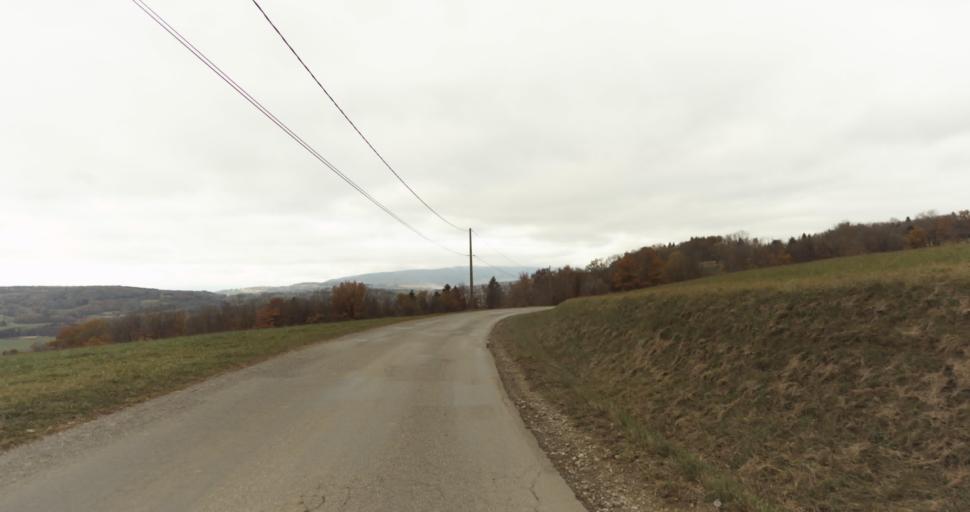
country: FR
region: Rhone-Alpes
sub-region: Departement de la Haute-Savoie
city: Saint-Martin-Bellevue
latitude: 45.9801
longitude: 6.1819
